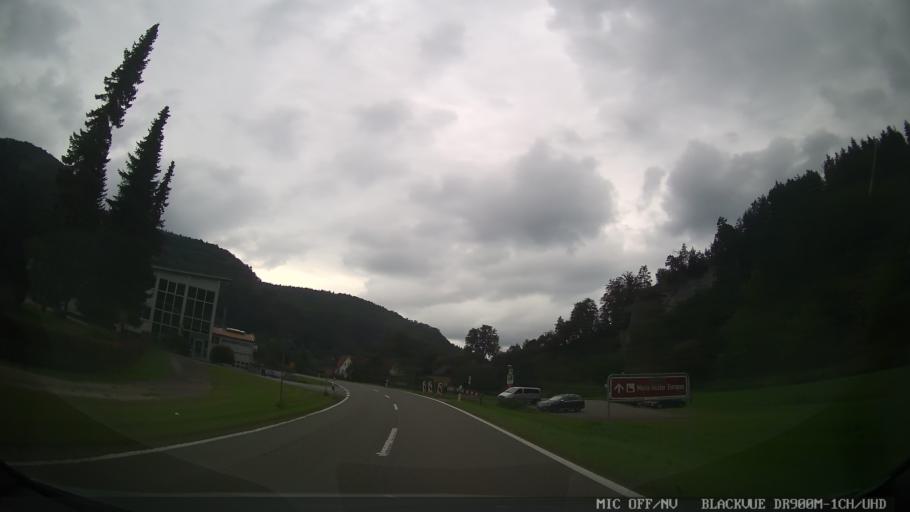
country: DE
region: Baden-Wuerttemberg
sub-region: Freiburg Region
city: Barenthal
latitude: 48.0736
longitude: 8.9260
